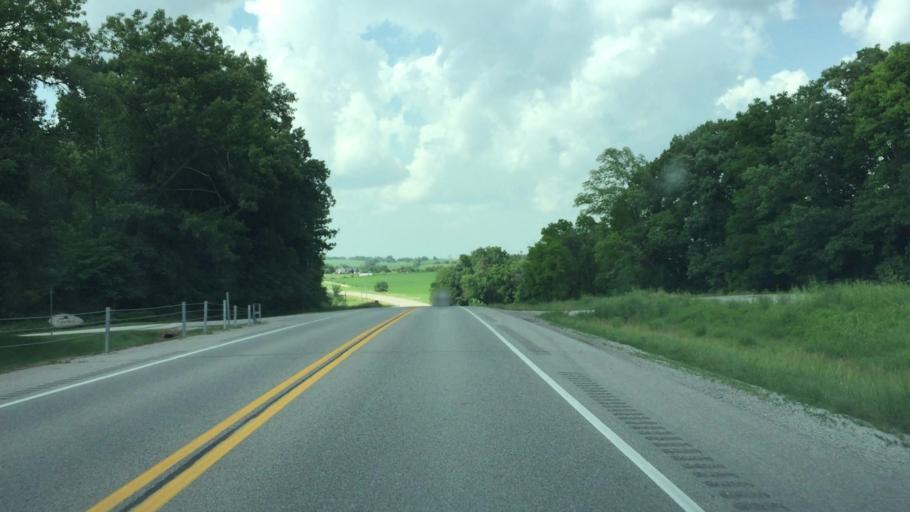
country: US
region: Iowa
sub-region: Johnson County
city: Solon
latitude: 41.7465
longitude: -91.4738
